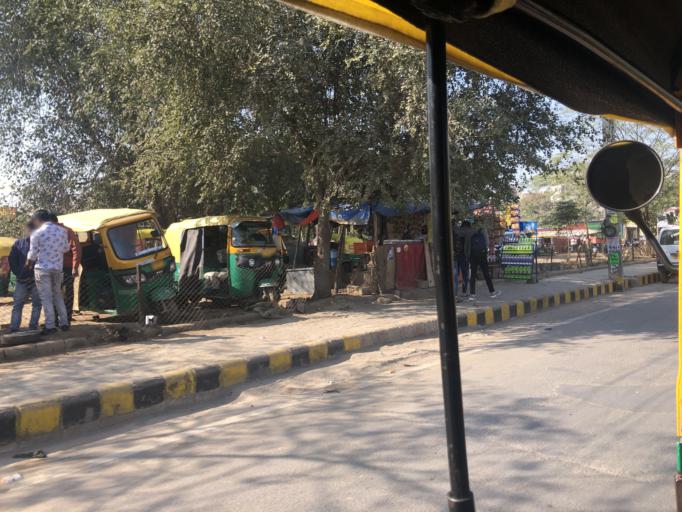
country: IN
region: Haryana
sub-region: Gurgaon
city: Gurgaon
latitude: 28.4479
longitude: 77.0740
